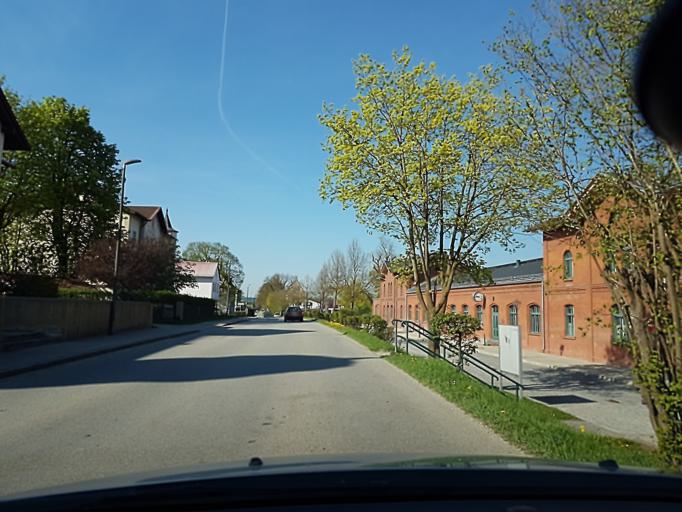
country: DE
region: Bavaria
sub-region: Upper Bavaria
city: Neumarkt-Sankt Veit
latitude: 48.3615
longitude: 12.5040
